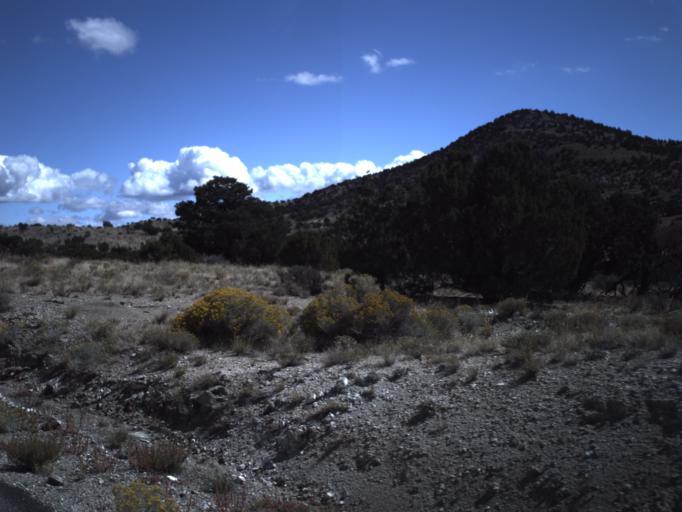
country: US
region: Utah
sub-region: Beaver County
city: Milford
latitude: 38.5164
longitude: -113.5549
